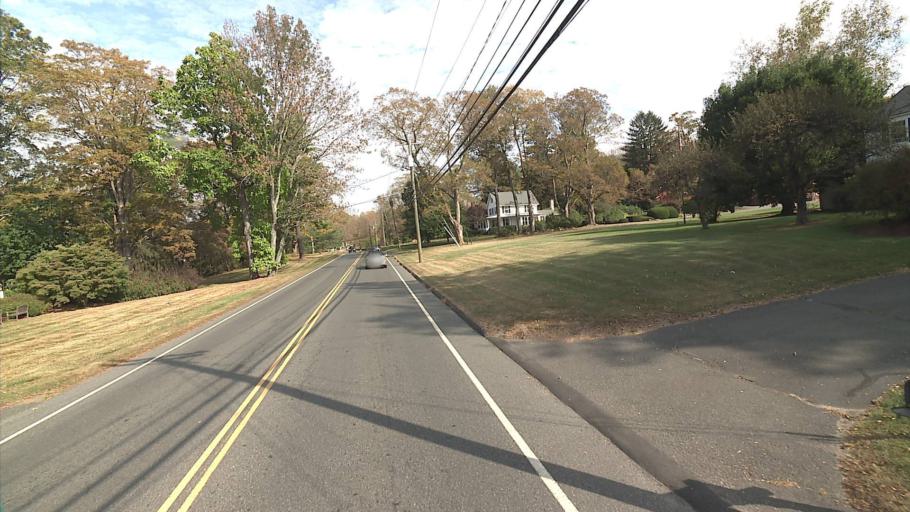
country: US
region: Connecticut
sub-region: New Haven County
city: Southbury
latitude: 41.4845
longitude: -73.2128
